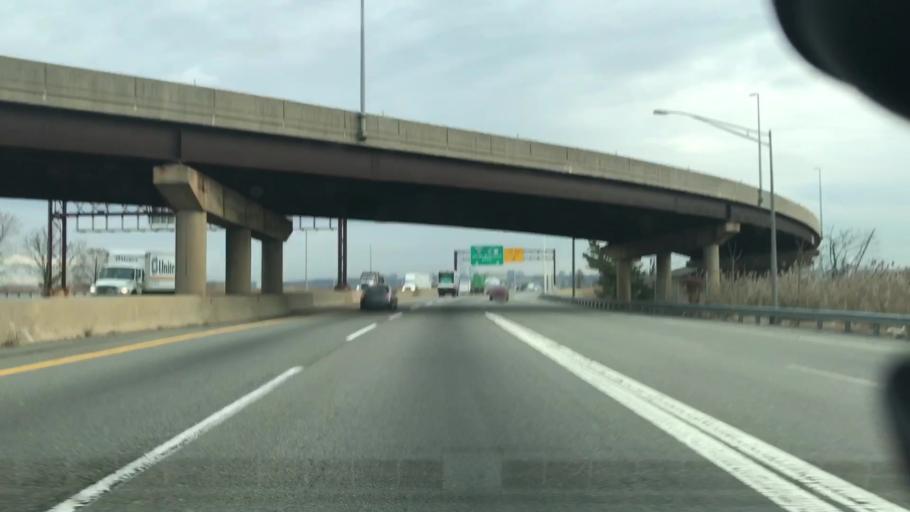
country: US
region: New Jersey
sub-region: Hudson County
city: Secaucus
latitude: 40.8134
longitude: -74.0563
